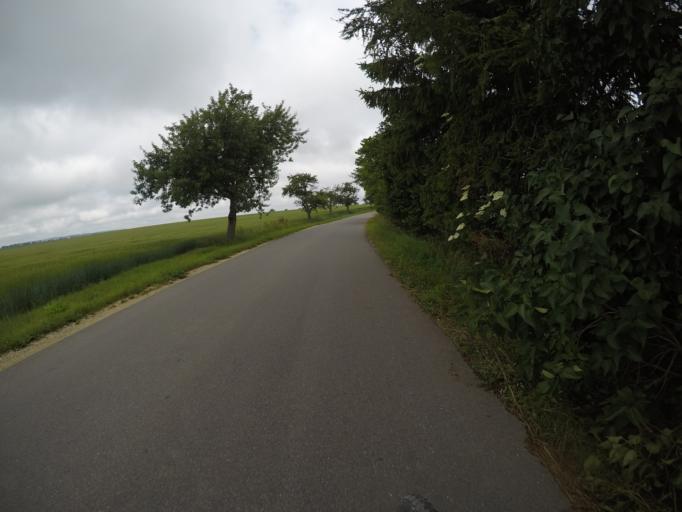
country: DE
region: Baden-Wuerttemberg
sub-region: Tuebingen Region
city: Dornstadt
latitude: 48.4874
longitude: 9.9527
